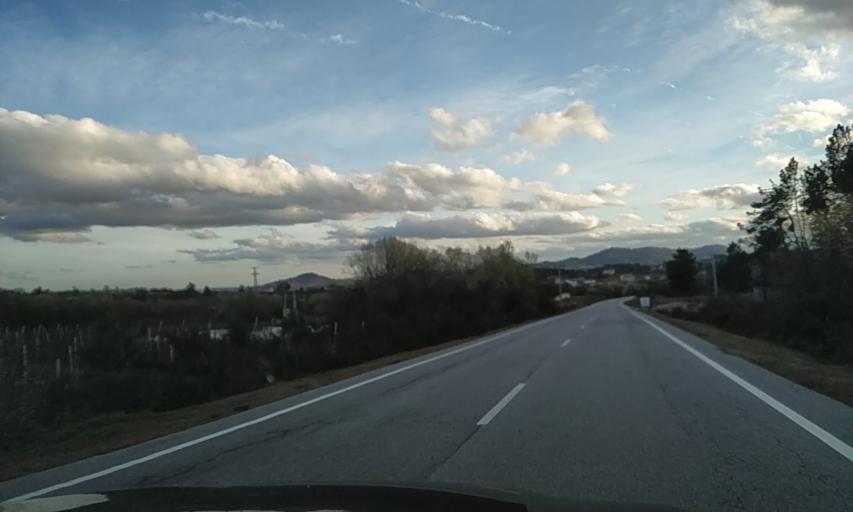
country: PT
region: Braganca
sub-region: Carrazeda de Ansiaes
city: Carrazeda de Anciaes
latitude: 41.2435
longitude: -7.3187
